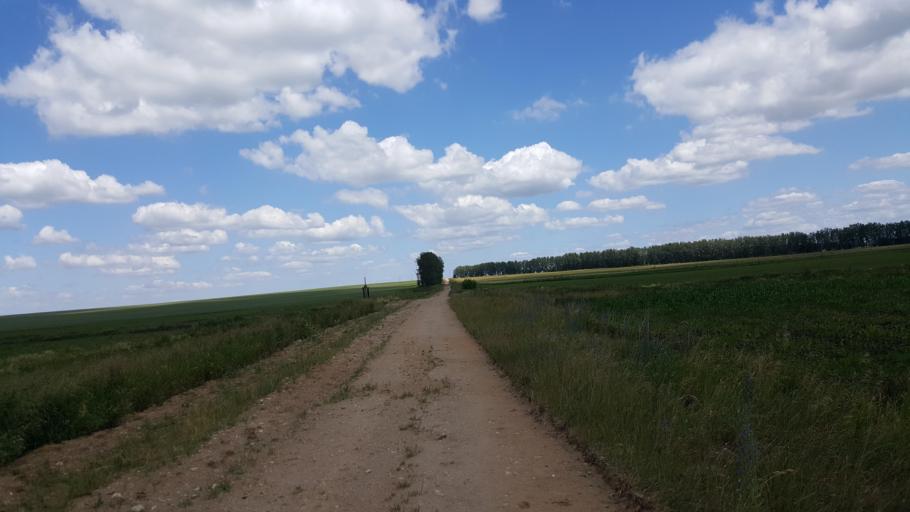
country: BY
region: Brest
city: Vysokaye
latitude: 52.4116
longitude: 23.5202
